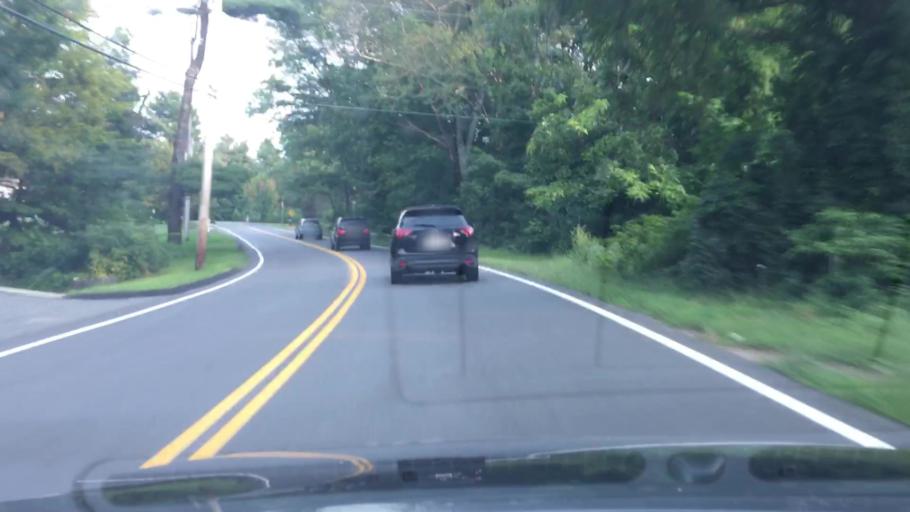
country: US
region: Massachusetts
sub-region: Worcester County
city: Westborough
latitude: 42.2446
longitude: -71.5816
